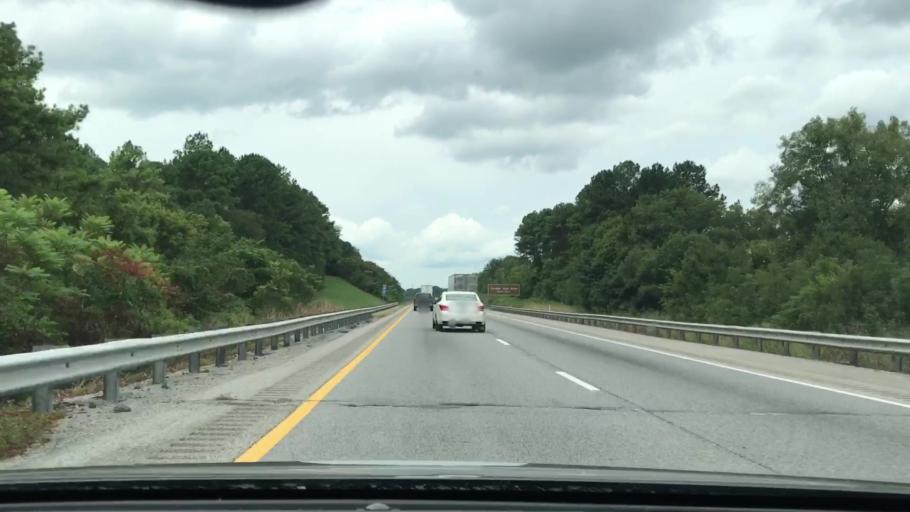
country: US
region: Tennessee
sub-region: Smith County
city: Gordonsville
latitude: 36.1719
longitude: -85.9106
